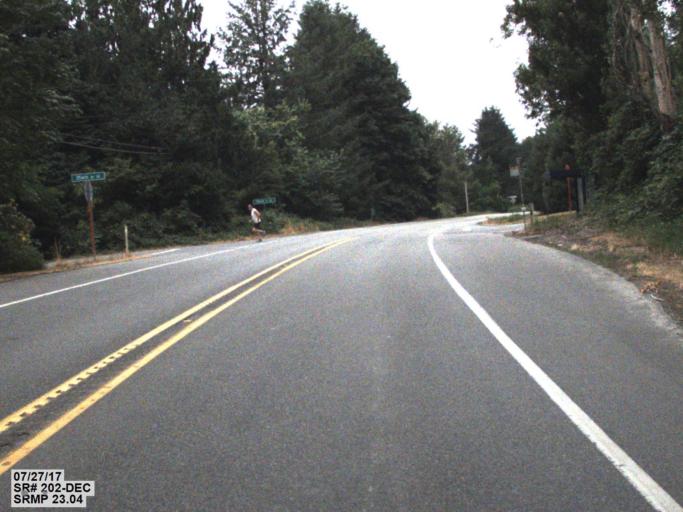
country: US
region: Washington
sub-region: King County
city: Fall City
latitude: 47.5624
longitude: -121.8652
